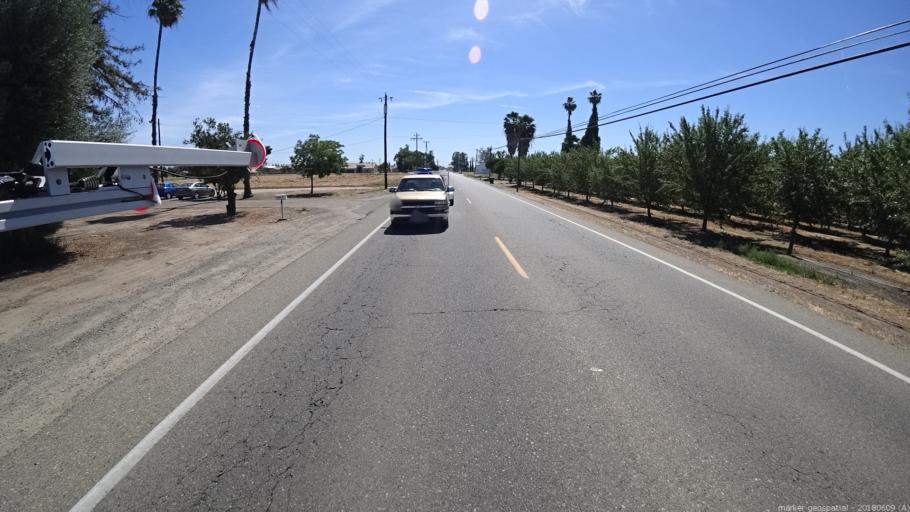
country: US
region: California
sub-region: Madera County
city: Madera
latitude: 36.9528
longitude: -120.1121
